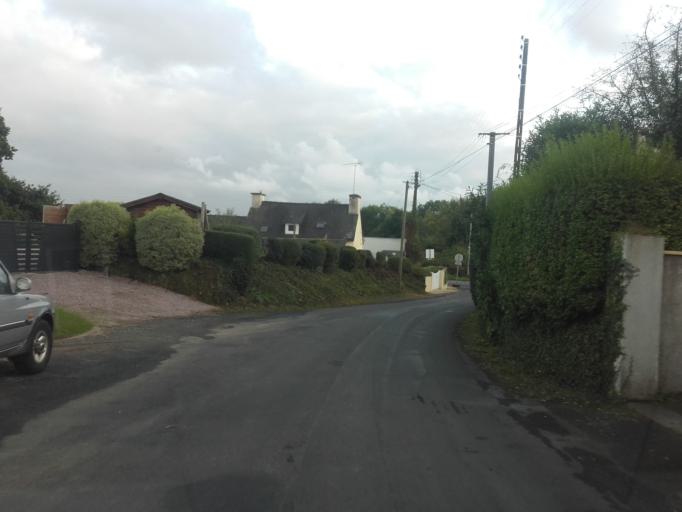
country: FR
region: Brittany
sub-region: Departement des Cotes-d'Armor
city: Plouha
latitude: 48.6726
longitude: -2.9321
